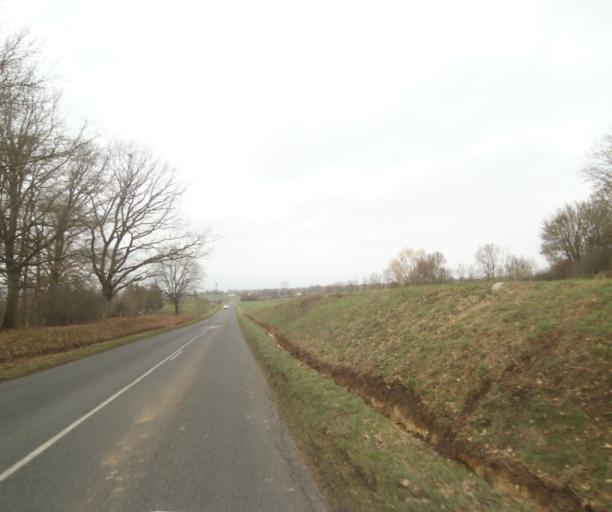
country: FR
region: Champagne-Ardenne
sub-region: Departement de la Marne
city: Pargny-sur-Saulx
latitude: 48.7404
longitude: 4.8528
